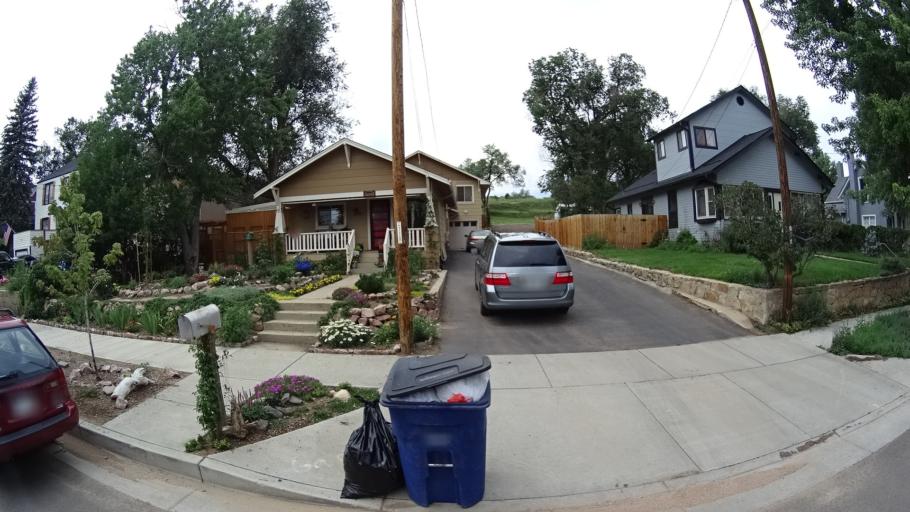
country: US
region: Colorado
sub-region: El Paso County
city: Colorado Springs
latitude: 38.8545
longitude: -104.8359
